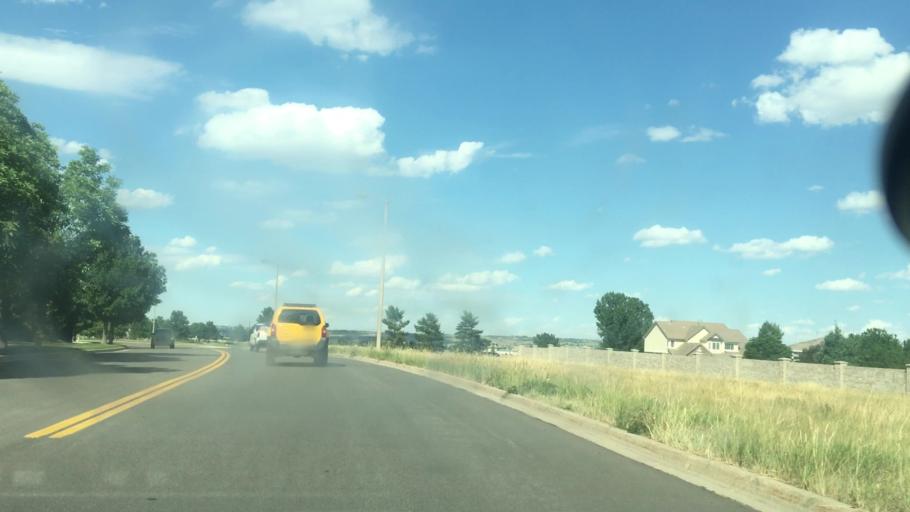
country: US
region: Colorado
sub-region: Douglas County
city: Meridian
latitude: 39.5334
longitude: -104.8450
